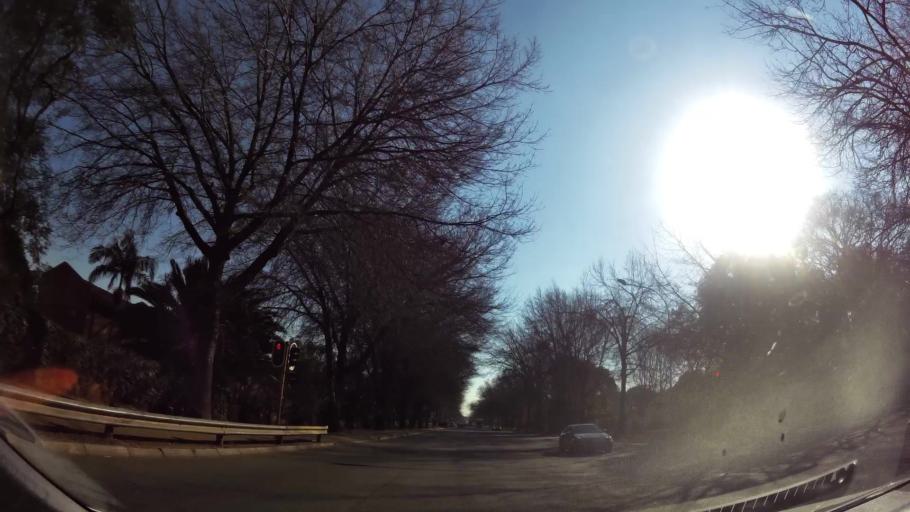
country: ZA
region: Gauteng
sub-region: Ekurhuleni Metropolitan Municipality
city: Germiston
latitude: -26.1865
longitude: 28.1360
